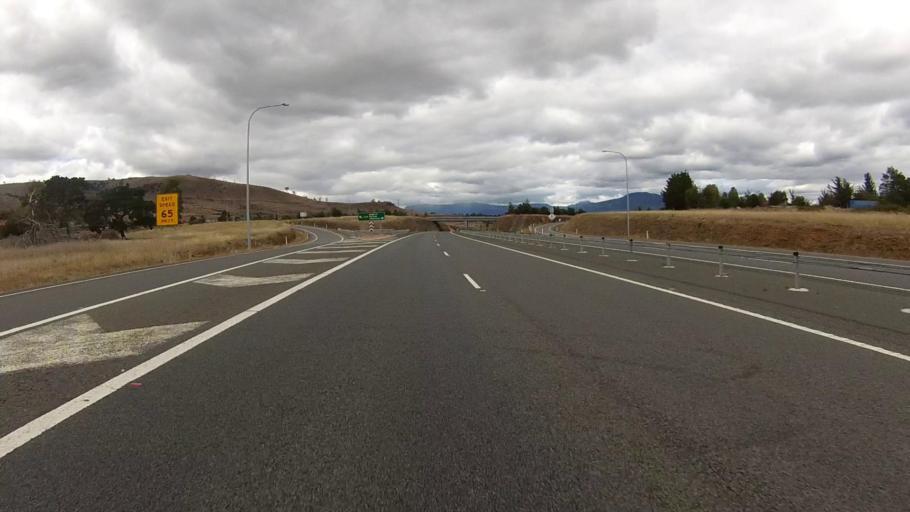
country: AU
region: Tasmania
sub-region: Brighton
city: Bridgewater
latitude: -42.6931
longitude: 147.2782
